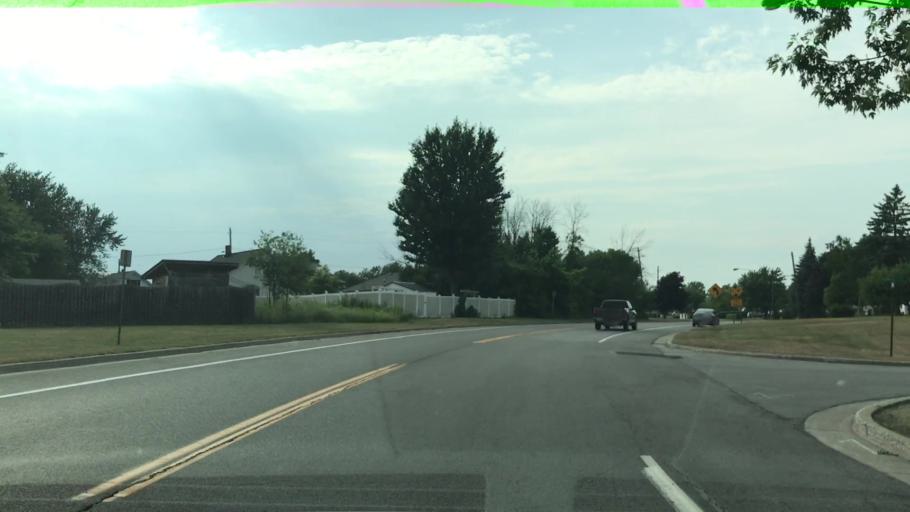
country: US
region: New York
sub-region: Erie County
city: Depew
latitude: 42.9150
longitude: -78.7092
